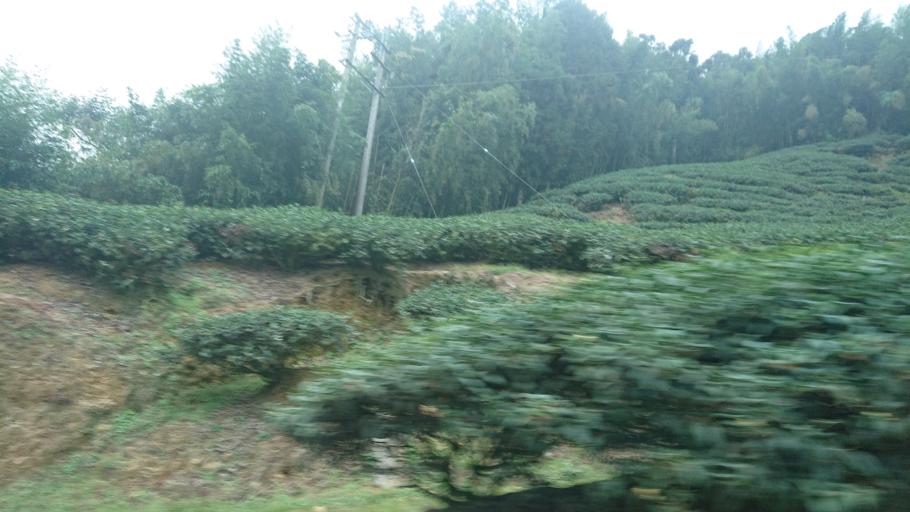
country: TW
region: Taiwan
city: Lugu
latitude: 23.6208
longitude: 120.7206
